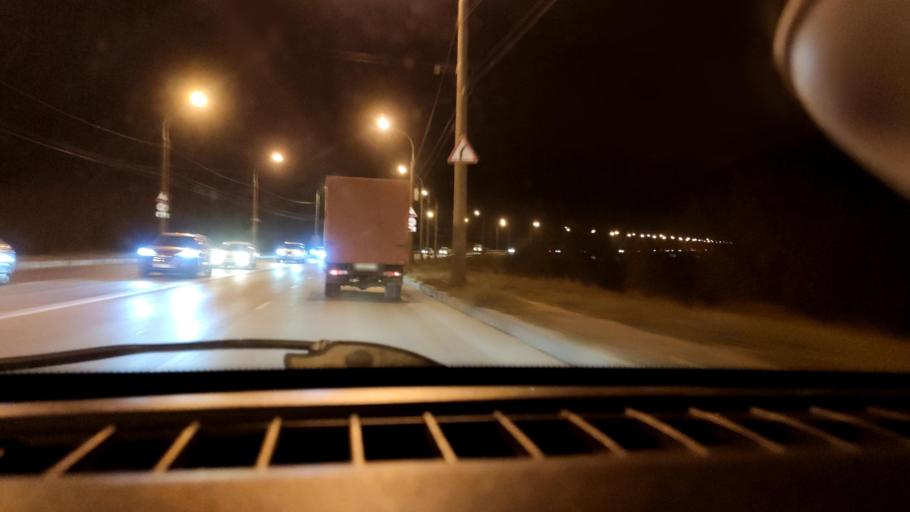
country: RU
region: Samara
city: Samara
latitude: 53.1666
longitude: 50.1966
